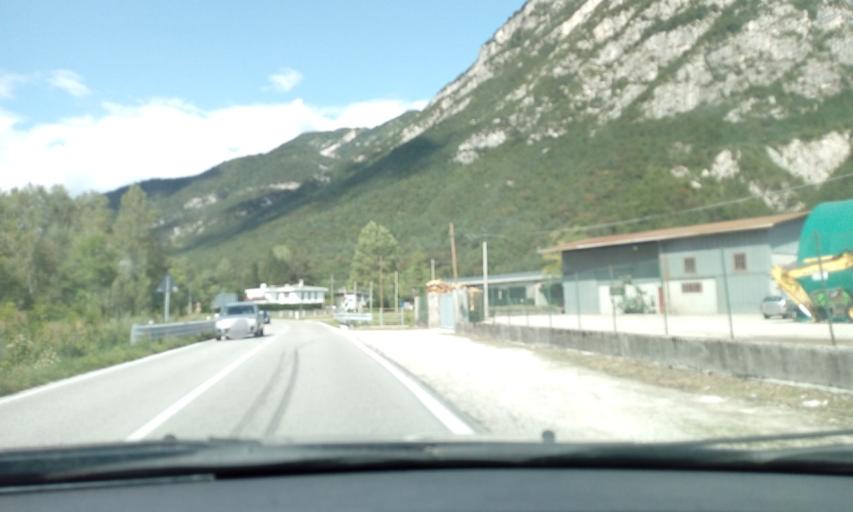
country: IT
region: Friuli Venezia Giulia
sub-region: Provincia di Udine
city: Trasaghis
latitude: 46.2868
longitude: 13.0636
